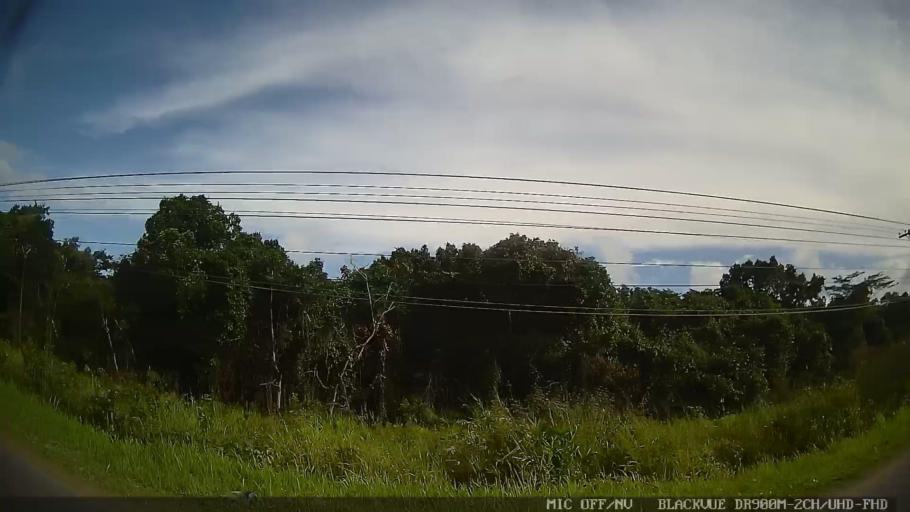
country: BR
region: Sao Paulo
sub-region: Itanhaem
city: Itanhaem
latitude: -24.1812
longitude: -46.8080
